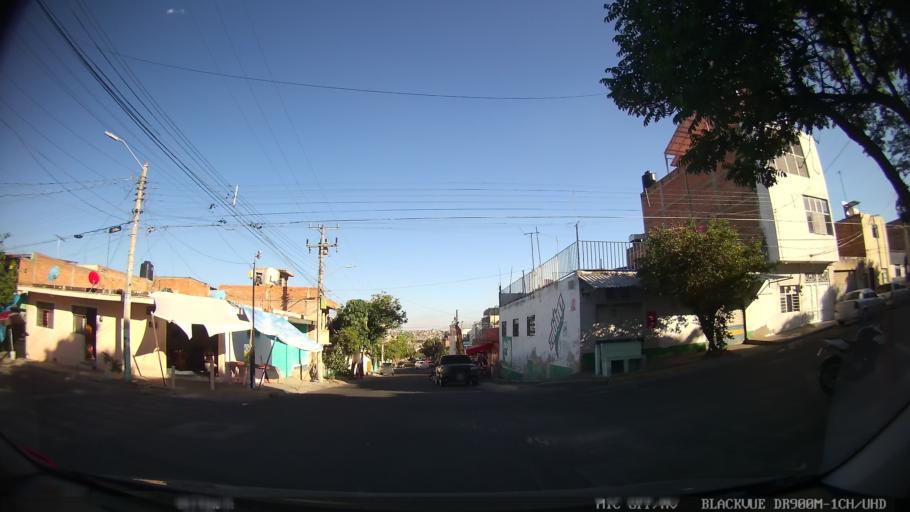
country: MX
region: Jalisco
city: Tlaquepaque
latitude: 20.7088
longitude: -103.2888
